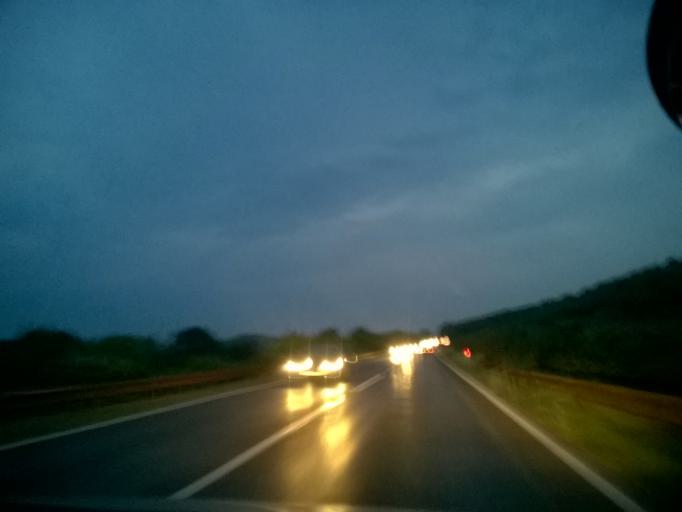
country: ME
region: Danilovgrad
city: Danilovgrad
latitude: 42.5032
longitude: 19.1432
